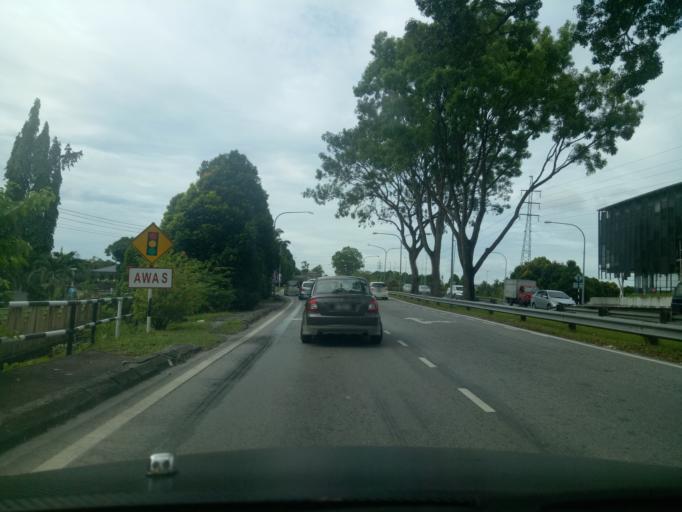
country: MY
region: Sarawak
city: Kuching
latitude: 1.5403
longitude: 110.3702
